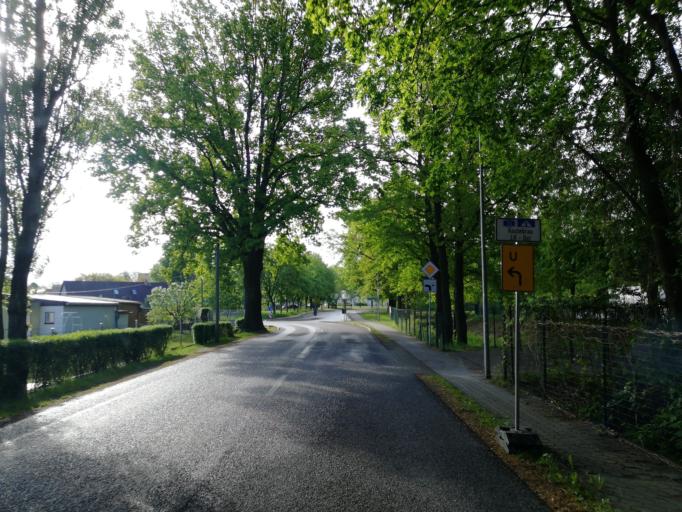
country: DE
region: Brandenburg
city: Lauchhammer
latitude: 51.5017
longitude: 13.7535
